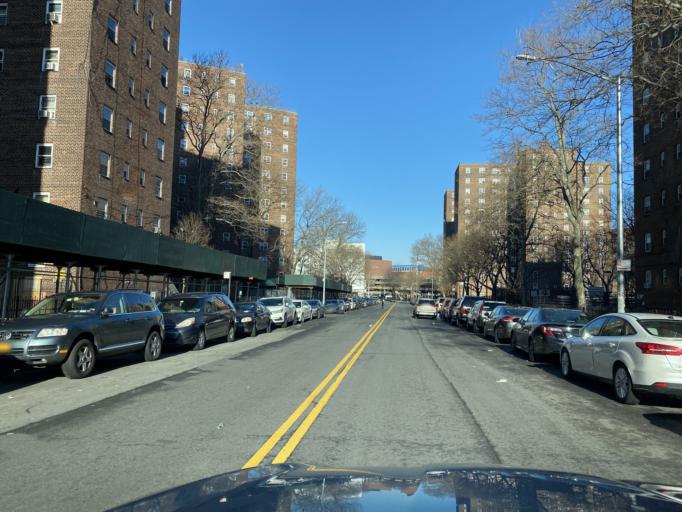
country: US
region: New York
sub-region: New York County
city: Inwood
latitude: 40.8136
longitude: -73.9231
